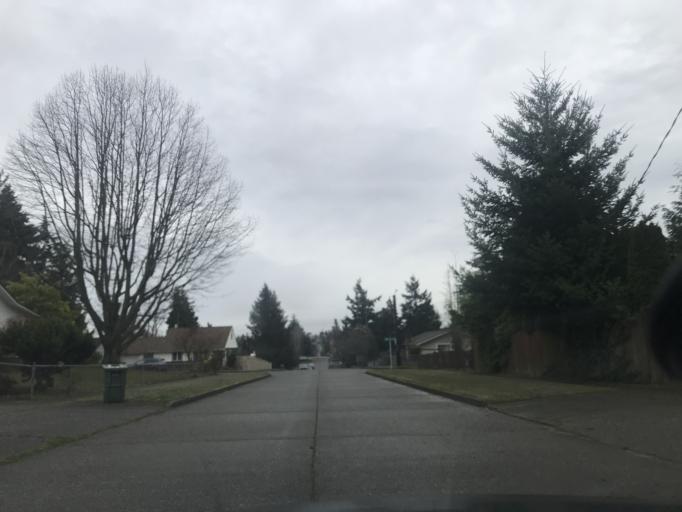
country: US
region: Washington
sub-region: King County
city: White Center
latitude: 47.5265
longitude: -122.3748
